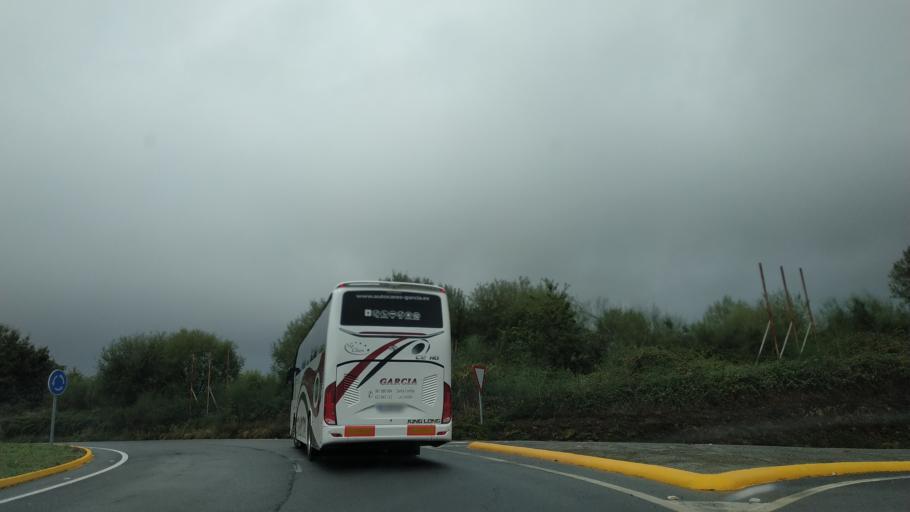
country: ES
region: Galicia
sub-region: Provincia da Coruna
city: Negreira
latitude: 42.9203
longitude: -8.7334
